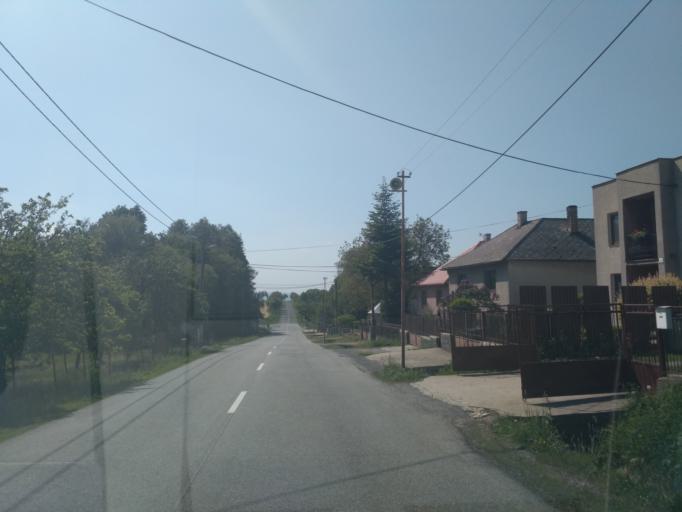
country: SK
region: Presovsky
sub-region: Okres Presov
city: Presov
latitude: 48.9169
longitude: 21.3234
